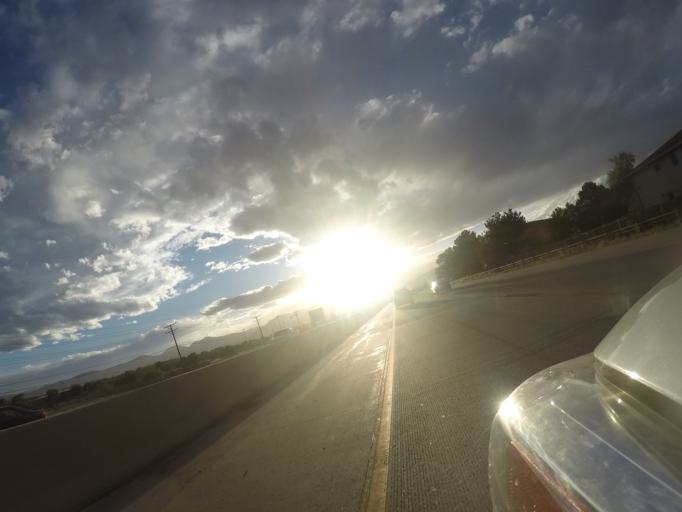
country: US
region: Colorado
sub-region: Jefferson County
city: Lakewood
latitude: 39.6535
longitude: -105.1000
